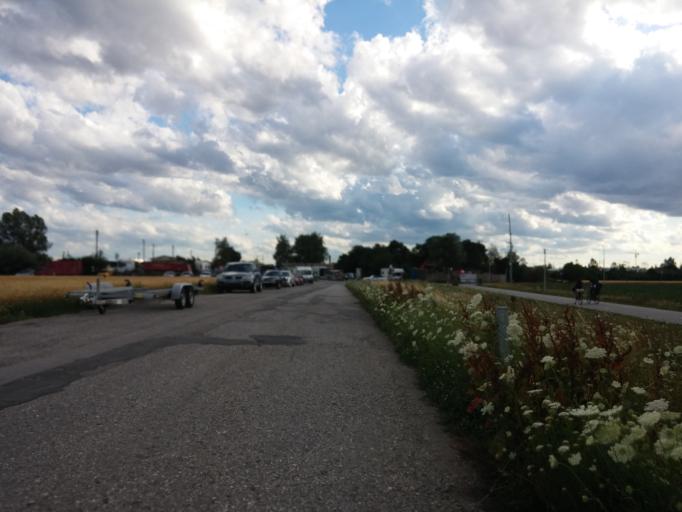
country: DE
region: Bavaria
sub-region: Upper Bavaria
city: Haar
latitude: 48.1232
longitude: 11.6886
